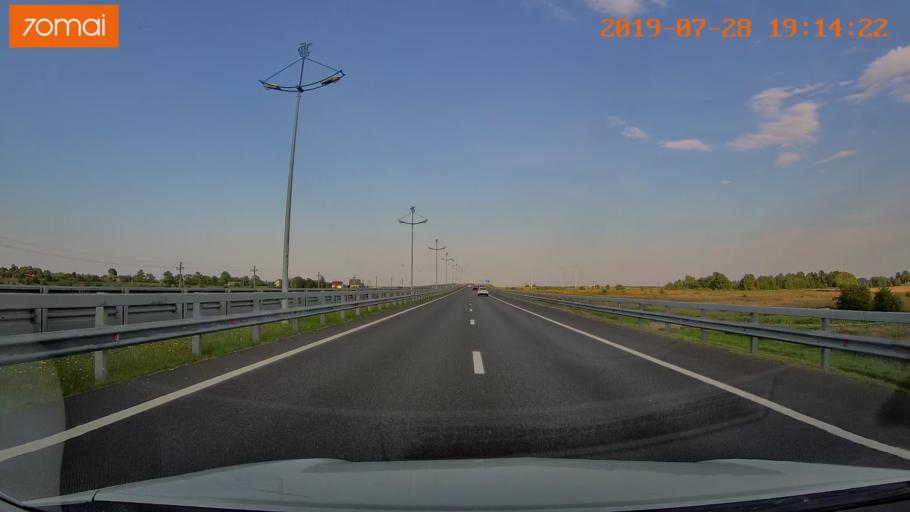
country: RU
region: Kaliningrad
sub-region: Gorod Kaliningrad
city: Pionerskiy
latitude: 54.9216
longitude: 20.3164
